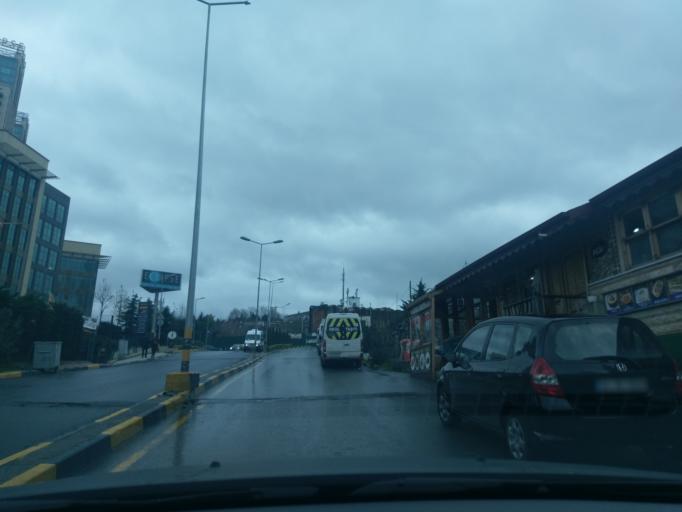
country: TR
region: Istanbul
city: Sisli
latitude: 41.1151
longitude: 29.0153
